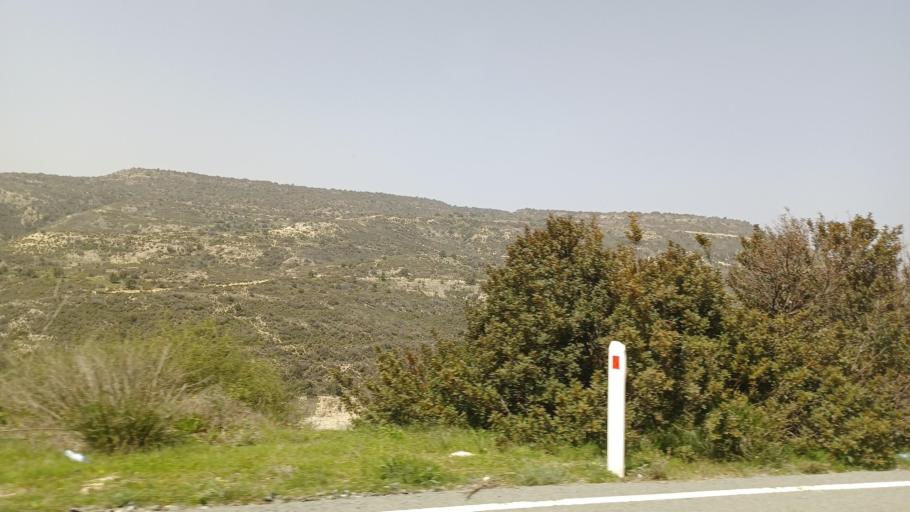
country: CY
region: Limassol
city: Pachna
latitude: 34.7600
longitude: 32.7445
